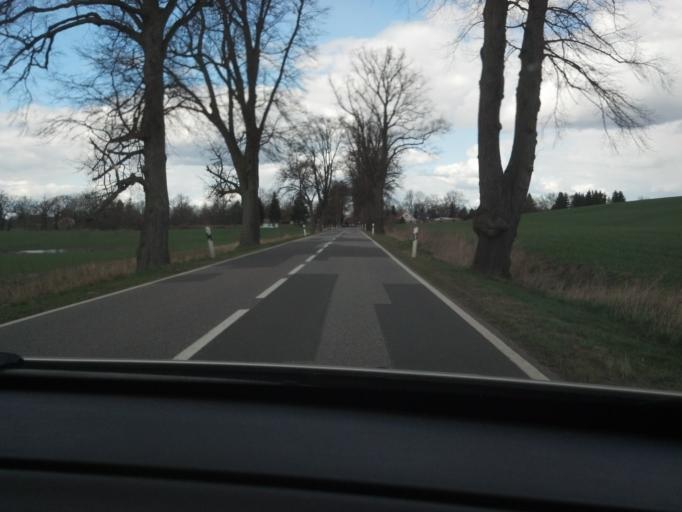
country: DE
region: Mecklenburg-Vorpommern
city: Loitz
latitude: 53.4171
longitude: 13.3590
